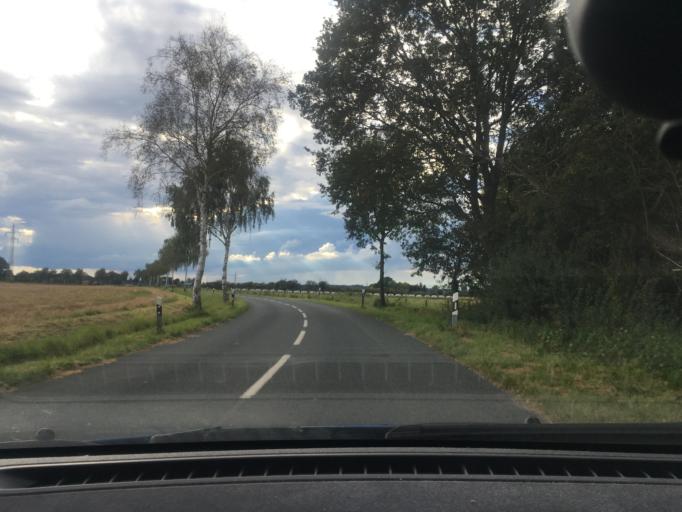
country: DE
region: Lower Saxony
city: Nahrendorf
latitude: 53.1626
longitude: 10.8250
